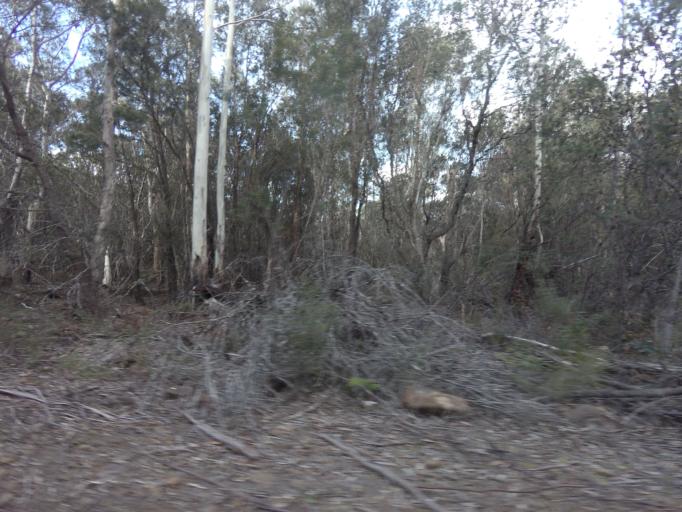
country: AU
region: Tasmania
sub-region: Break O'Day
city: St Helens
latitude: -41.8447
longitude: 148.0906
